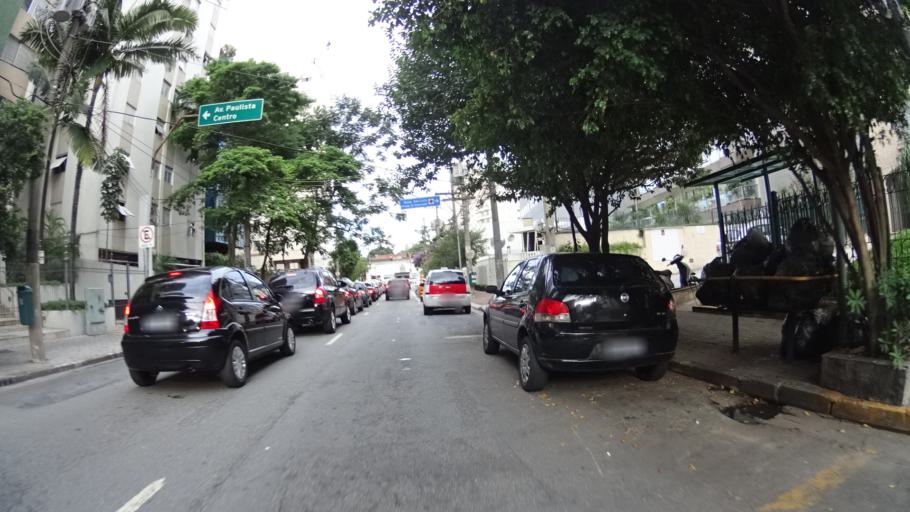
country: BR
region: Sao Paulo
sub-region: Sao Paulo
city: Sao Paulo
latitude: -23.5801
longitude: -46.6718
